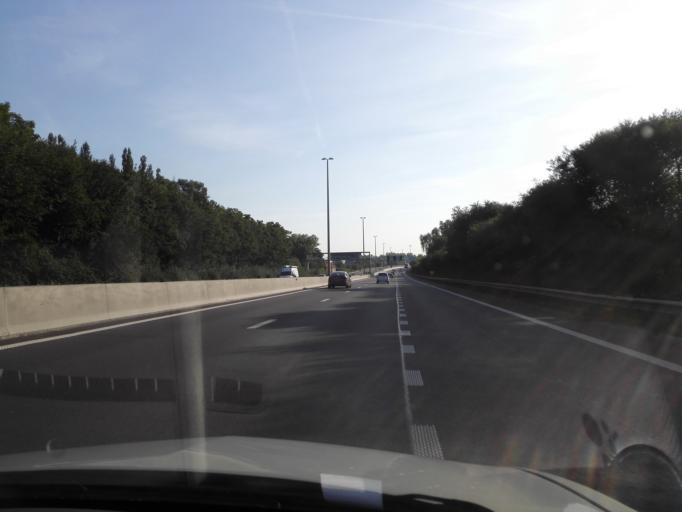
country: BE
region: Flanders
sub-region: Provincie Vlaams-Brabant
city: Leuven
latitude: 50.8974
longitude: 4.6945
